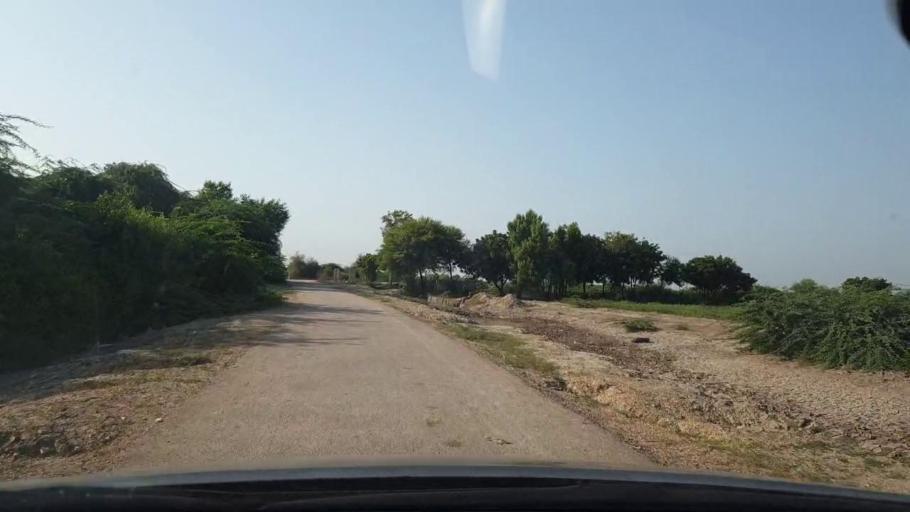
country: PK
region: Sindh
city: Naukot
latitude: 24.8390
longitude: 69.2224
